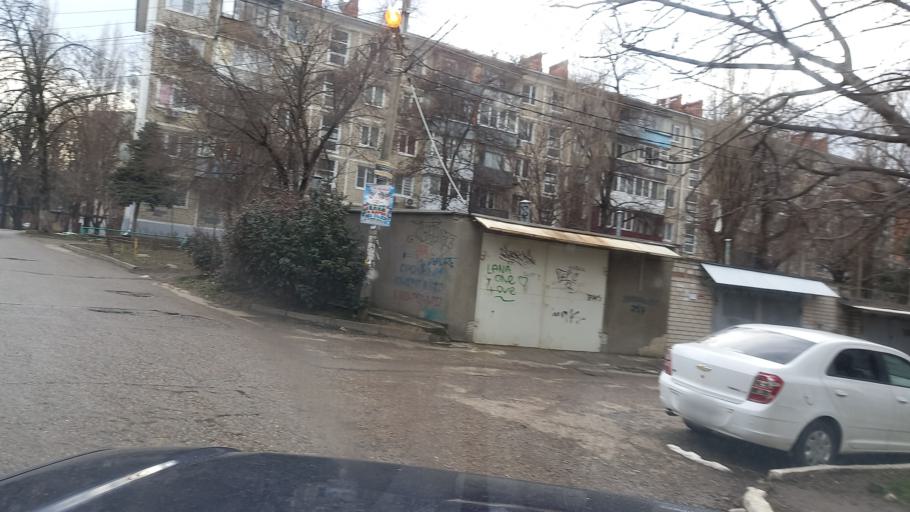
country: RU
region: Krasnodarskiy
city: Pashkovskiy
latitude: 45.0185
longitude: 39.0404
